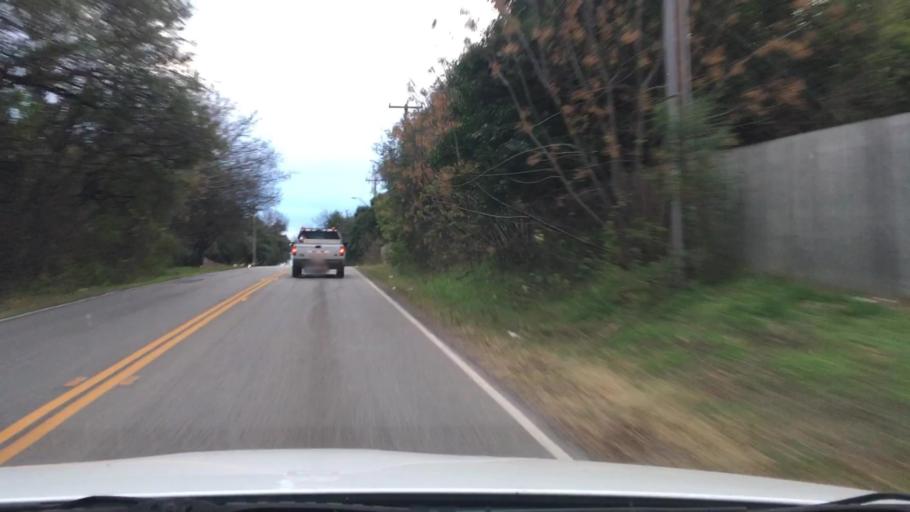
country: US
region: Texas
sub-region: Bexar County
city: Live Oak
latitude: 29.5929
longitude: -98.3583
